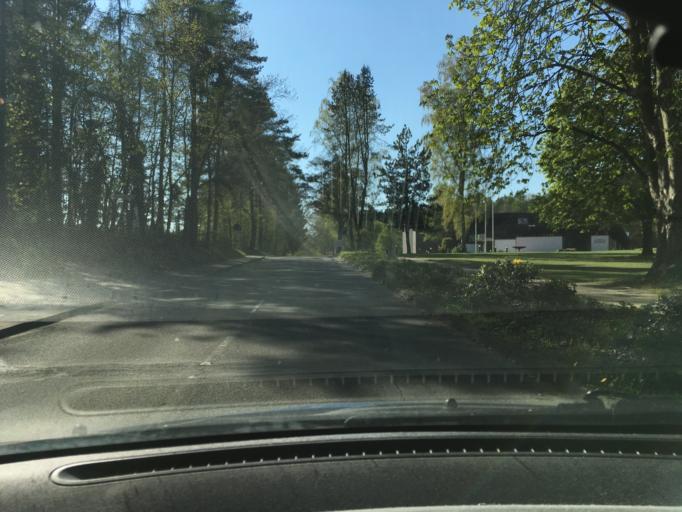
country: DE
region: Lower Saxony
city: Hitzacker
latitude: 53.1554
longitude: 11.0403
